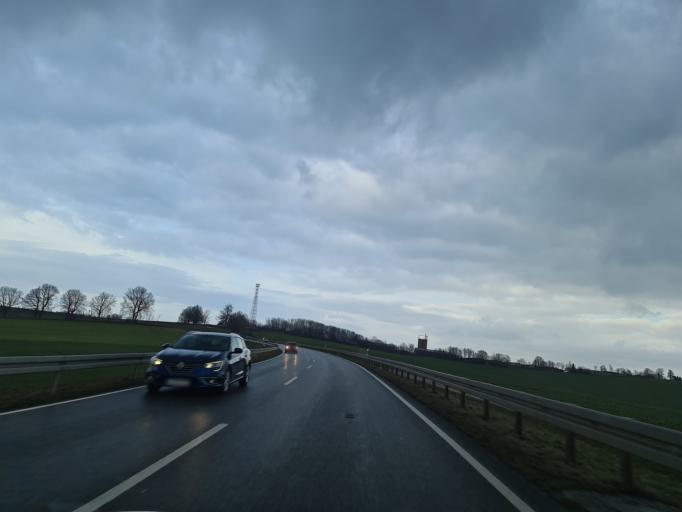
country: DE
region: Saxony
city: Reinsdorf
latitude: 50.6877
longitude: 12.5936
